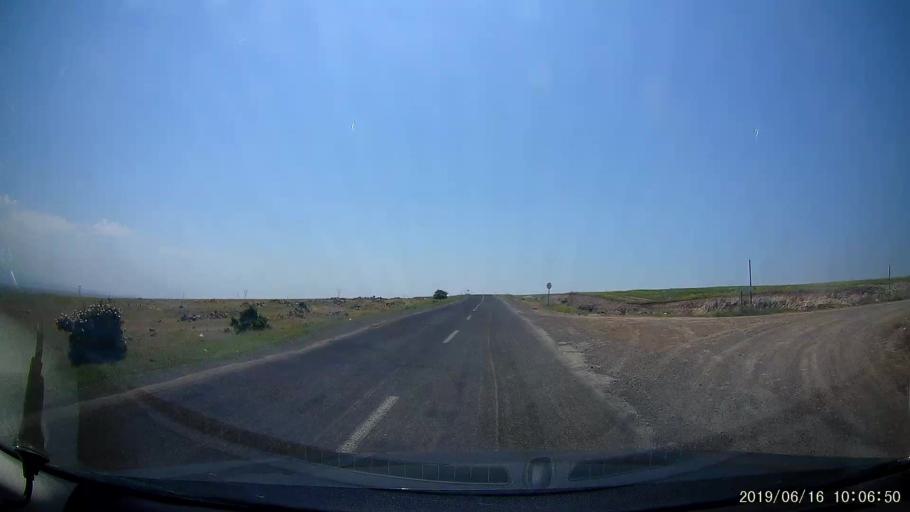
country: TR
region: Kars
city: Digor
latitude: 40.2507
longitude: 43.5474
